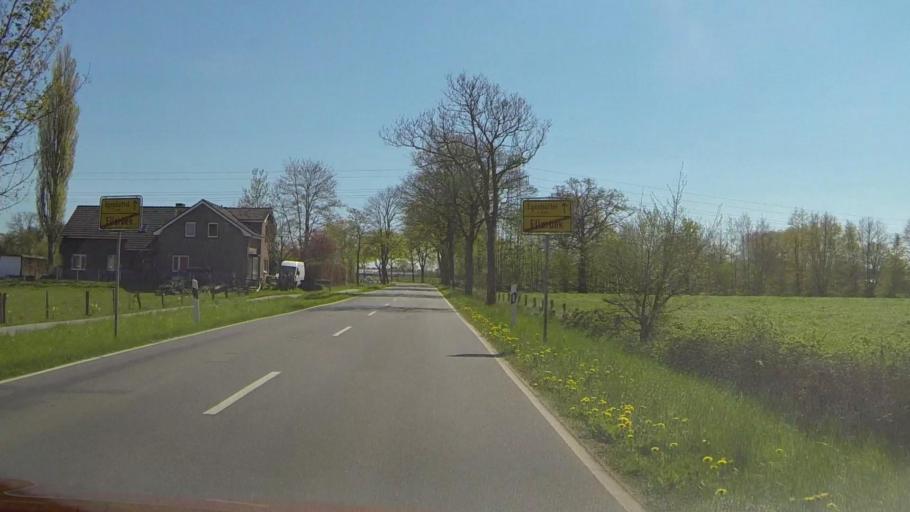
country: DE
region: Schleswig-Holstein
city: Ellerbek
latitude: 53.6529
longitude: 9.8699
